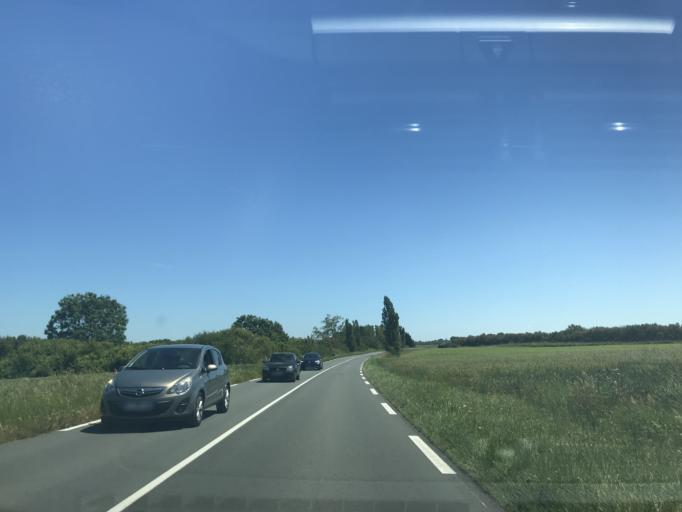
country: FR
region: Poitou-Charentes
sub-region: Departement de la Charente-Maritime
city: Meschers-sur-Gironde
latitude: 45.5532
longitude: -0.9182
